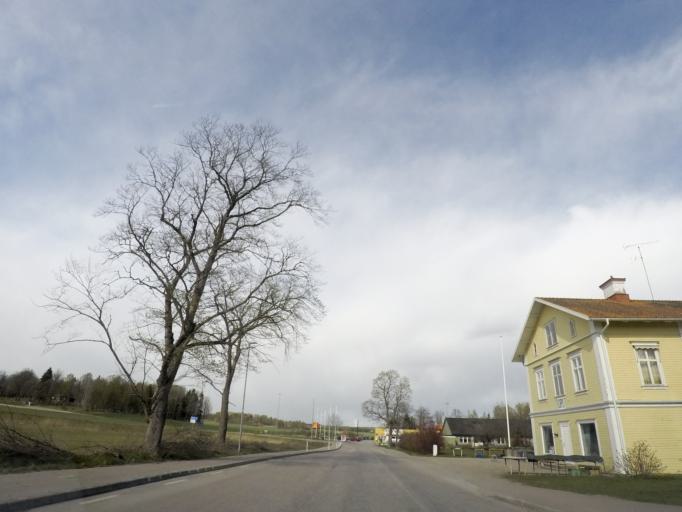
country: SE
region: Soedermanland
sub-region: Katrineholms Kommun
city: Katrineholm
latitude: 59.1484
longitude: 16.0664
